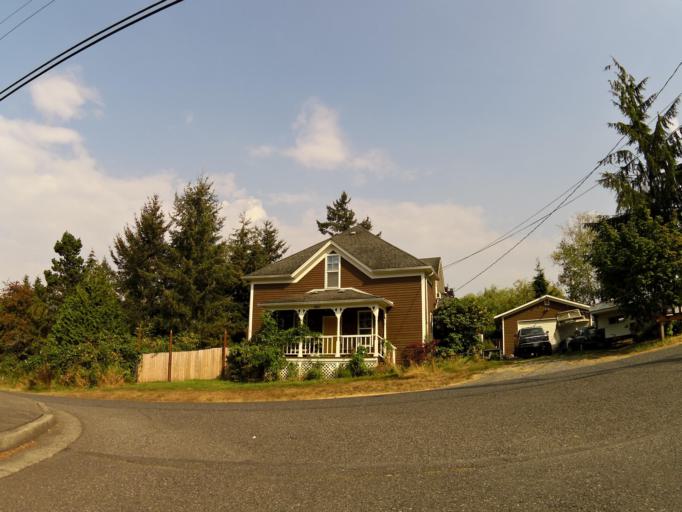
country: US
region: Washington
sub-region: Whatcom County
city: Bellingham
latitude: 48.7151
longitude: -122.4919
